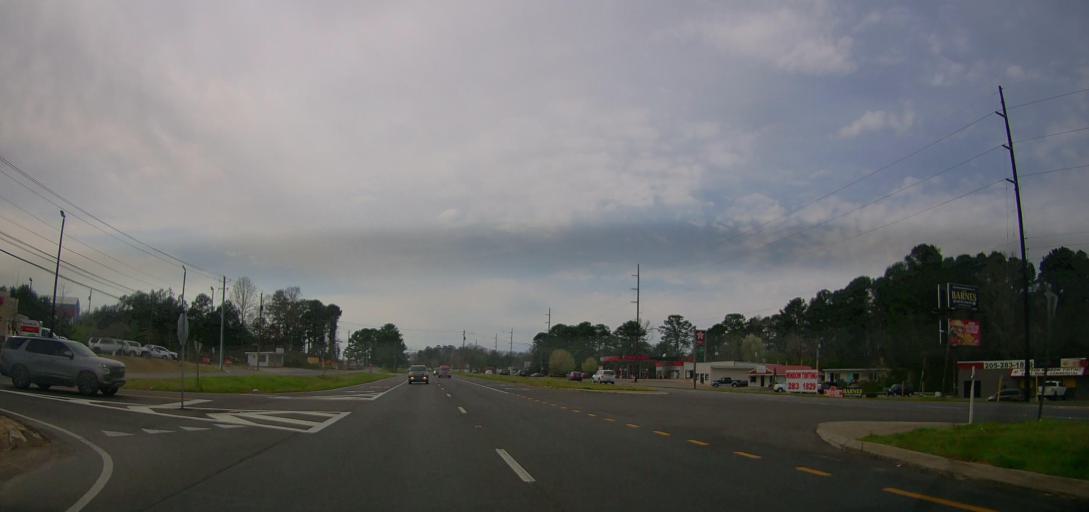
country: US
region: Alabama
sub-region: Walker County
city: Jasper
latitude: 33.8394
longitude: -87.2326
